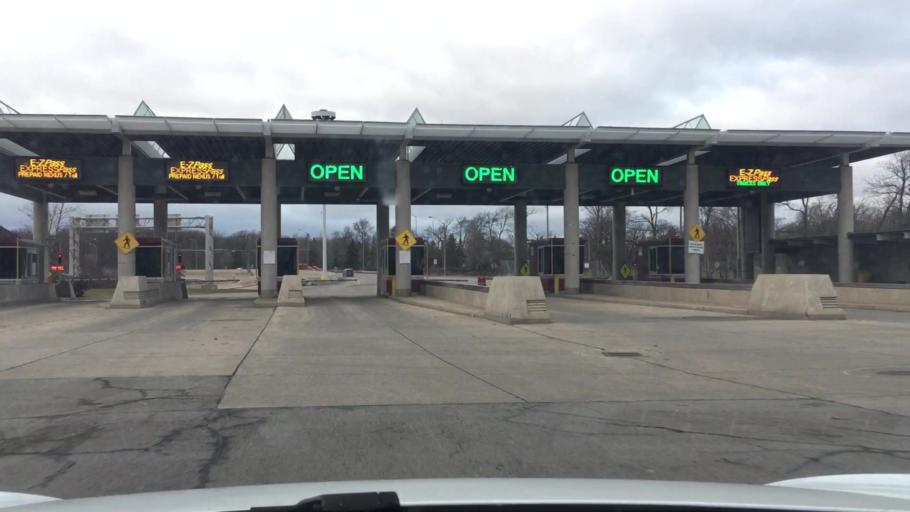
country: US
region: New York
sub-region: Niagara County
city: Lewiston
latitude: 43.1566
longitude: -79.0521
